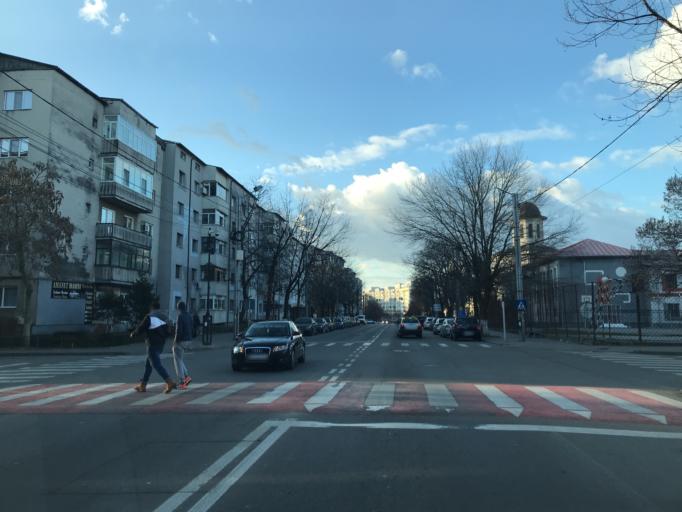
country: RO
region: Olt
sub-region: Municipiul Slatina
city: Slatina
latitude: 44.4245
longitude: 24.3790
